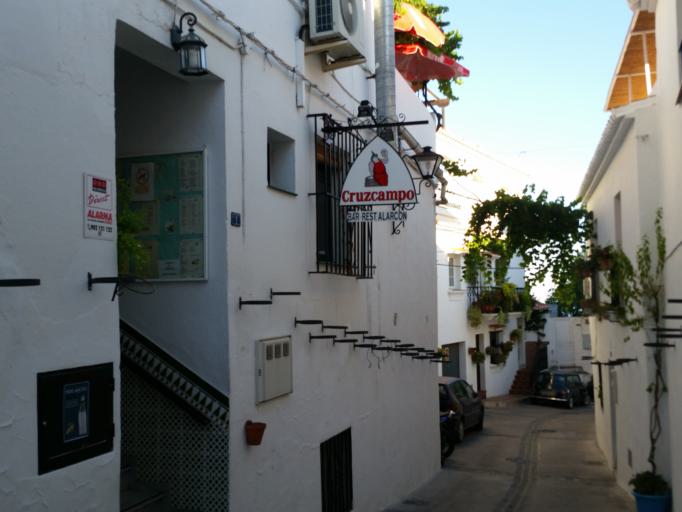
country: ES
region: Andalusia
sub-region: Provincia de Malaga
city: Mijas
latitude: 36.5937
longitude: -4.6435
